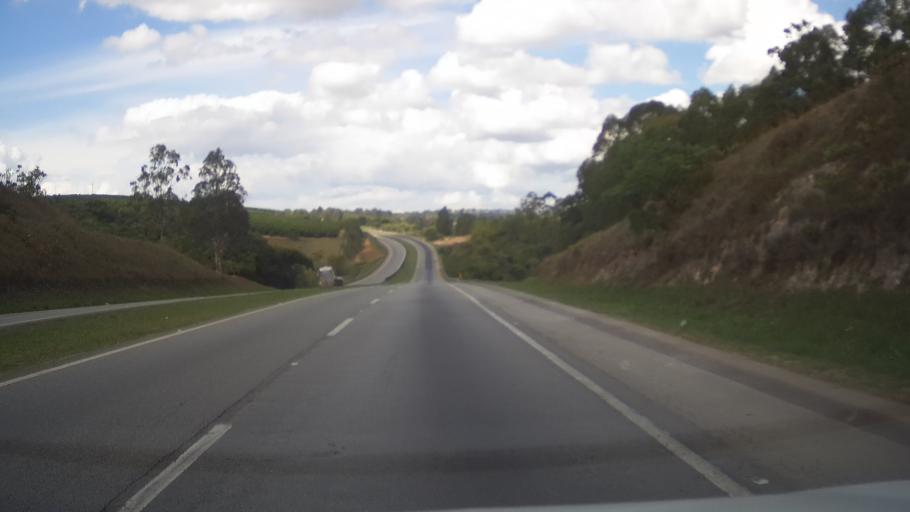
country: BR
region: Minas Gerais
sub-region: Santo Antonio Do Amparo
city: Santo Antonio do Amparo
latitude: -20.8466
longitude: -44.8320
